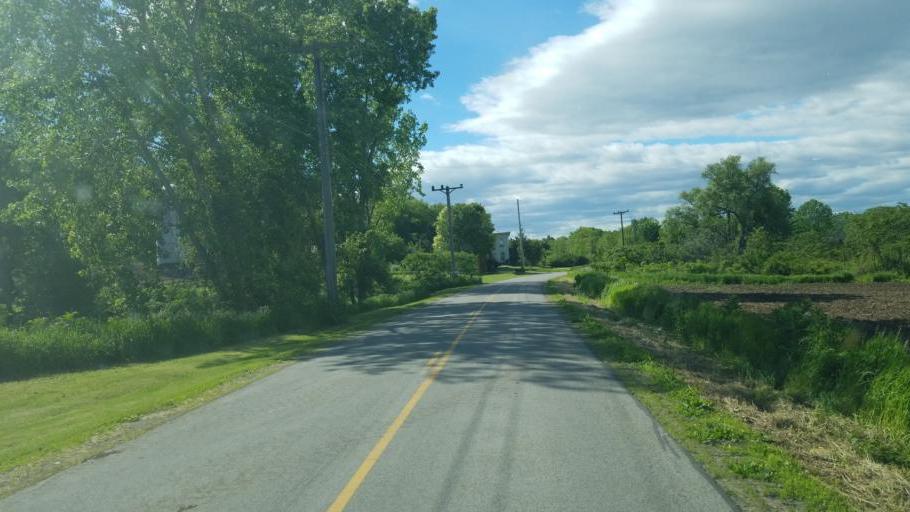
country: US
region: New York
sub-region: Montgomery County
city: Saint Johnsville
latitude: 42.9702
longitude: -74.6490
